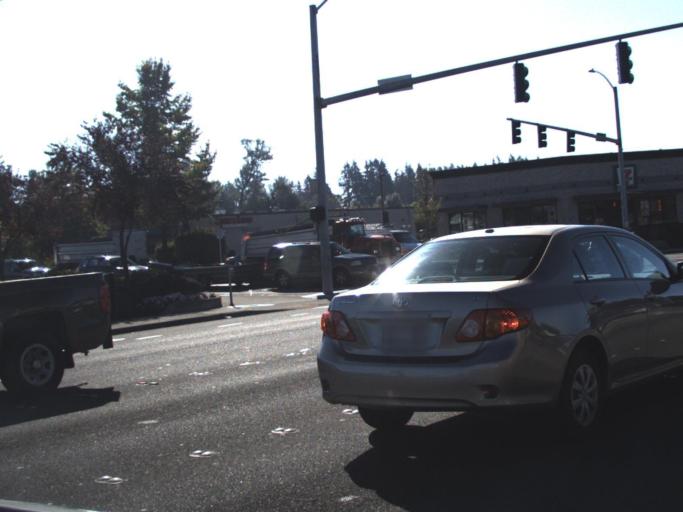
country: US
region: Washington
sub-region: King County
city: Kent
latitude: 47.3871
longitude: -122.2022
